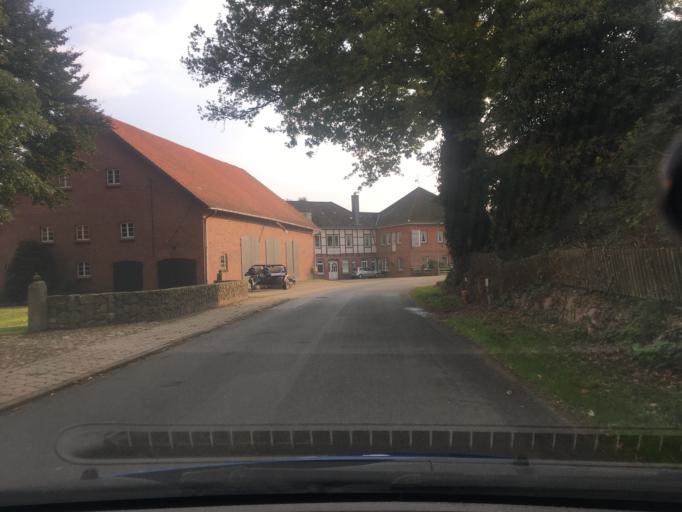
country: DE
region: Lower Saxony
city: Eyendorf
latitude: 53.2016
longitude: 10.1529
